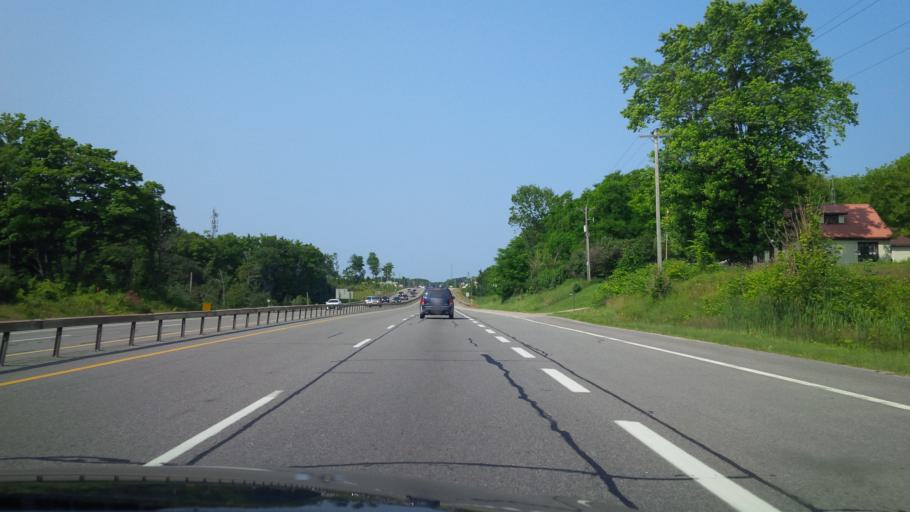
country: CA
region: Ontario
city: Orillia
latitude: 44.5058
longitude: -79.4786
